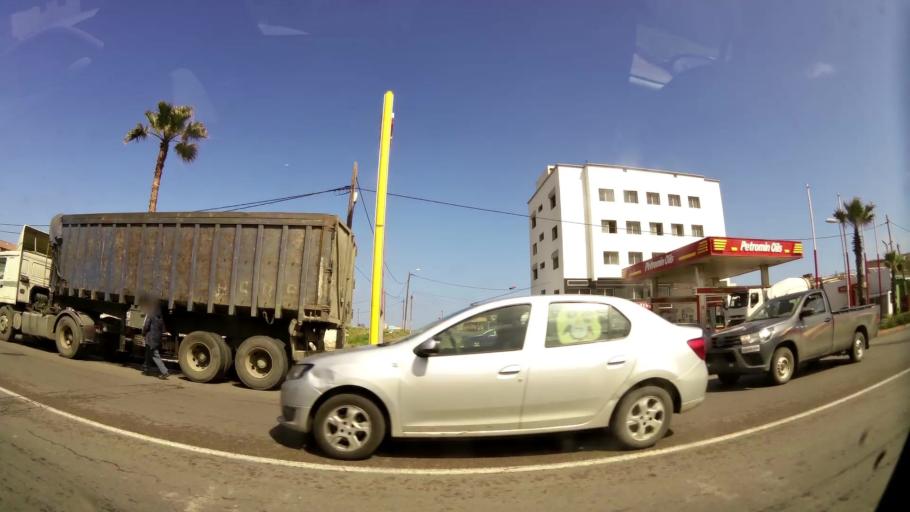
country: MA
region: Grand Casablanca
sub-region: Mediouna
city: Tit Mellil
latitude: 33.6207
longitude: -7.5318
